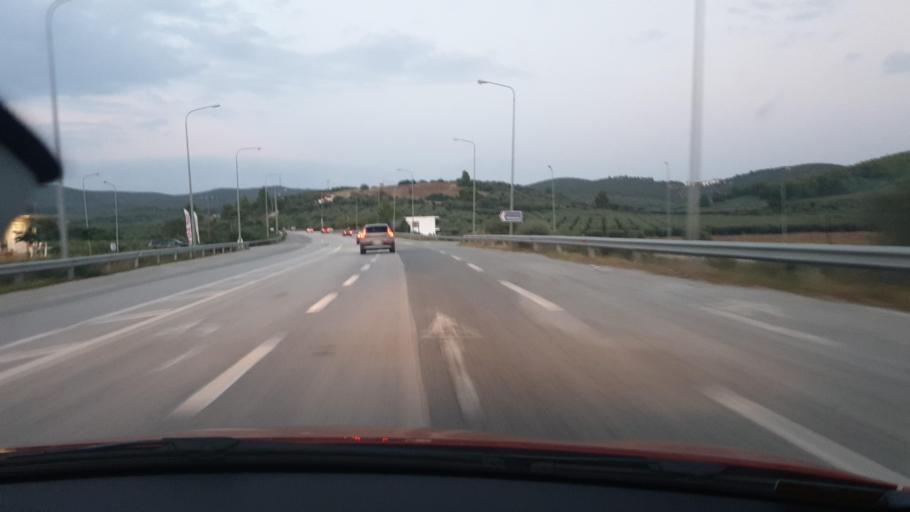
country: GR
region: Central Macedonia
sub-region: Nomos Chalkidikis
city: Ormylia
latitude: 40.2526
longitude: 23.5504
